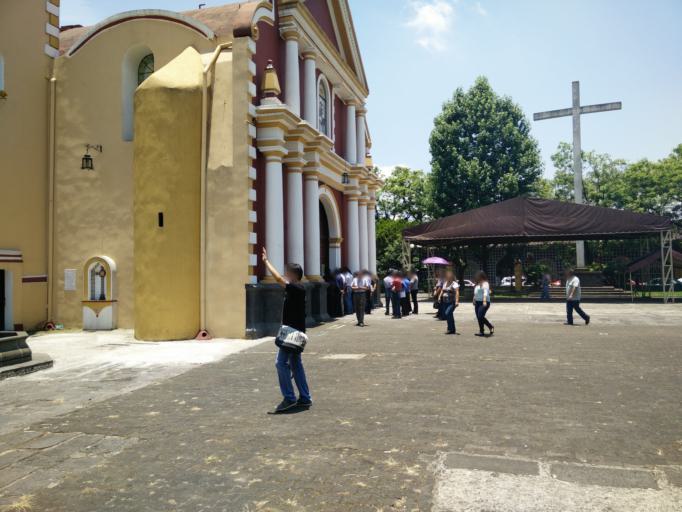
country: MX
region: Veracruz
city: Coatepec
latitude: 19.4542
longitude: -96.9590
